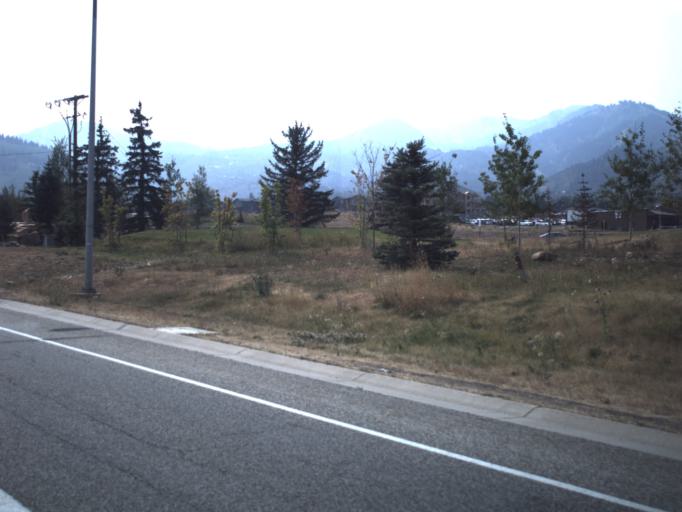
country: US
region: Utah
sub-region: Summit County
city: Snyderville
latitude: 40.6887
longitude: -111.5443
